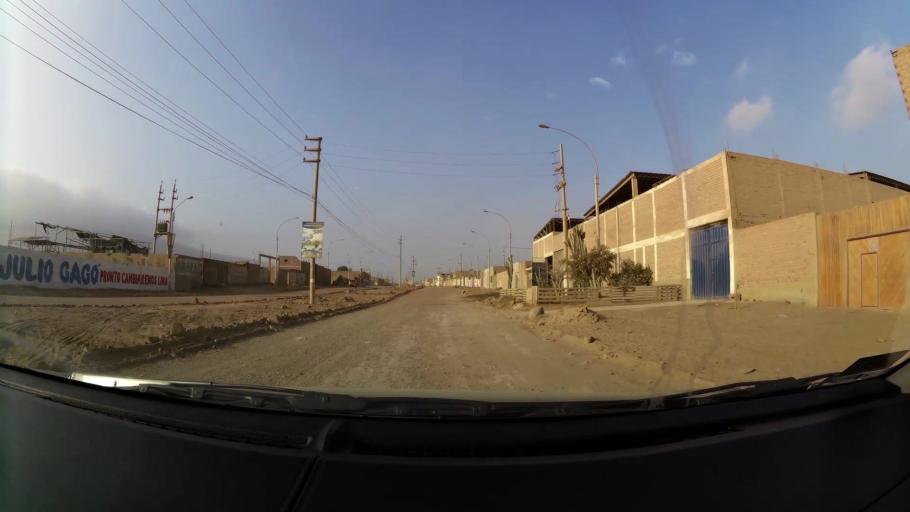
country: PE
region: Lima
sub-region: Lima
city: Santa Rosa
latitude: -11.7601
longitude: -77.1588
